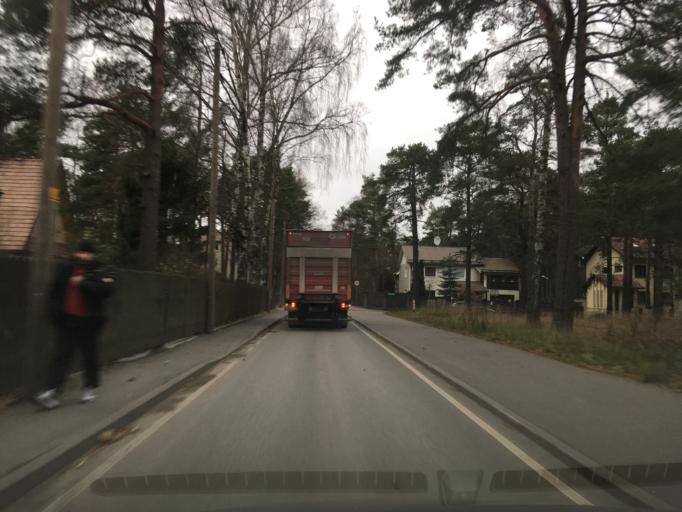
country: EE
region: Harju
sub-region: Saue vald
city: Laagri
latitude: 59.3783
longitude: 24.6762
